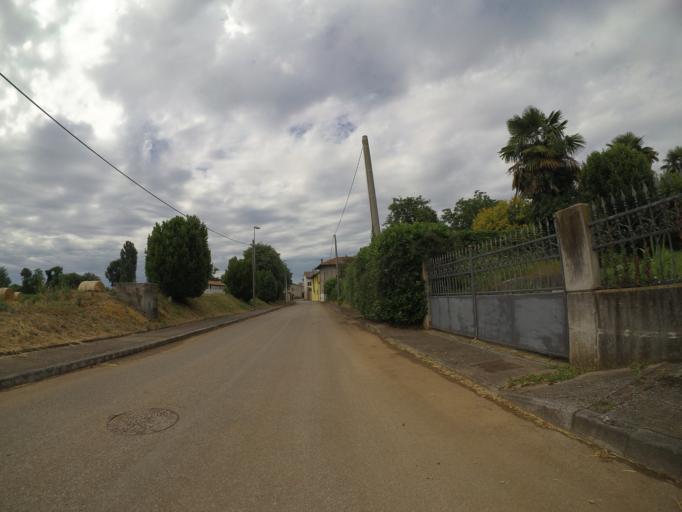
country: IT
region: Friuli Venezia Giulia
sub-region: Provincia di Udine
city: Bertiolo
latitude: 45.9564
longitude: 13.0899
